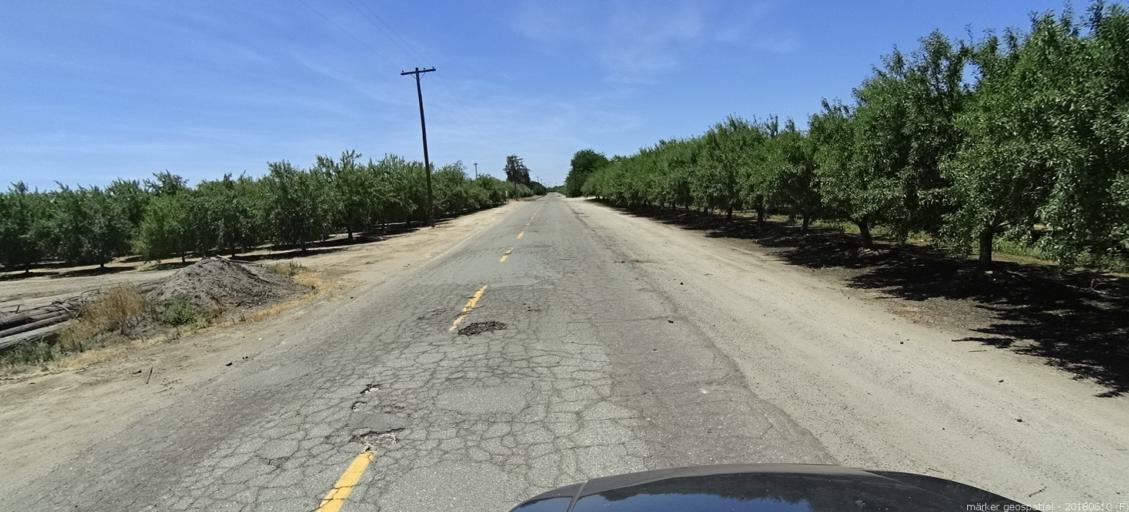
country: US
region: California
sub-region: Madera County
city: Chowchilla
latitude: 37.0617
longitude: -120.3002
